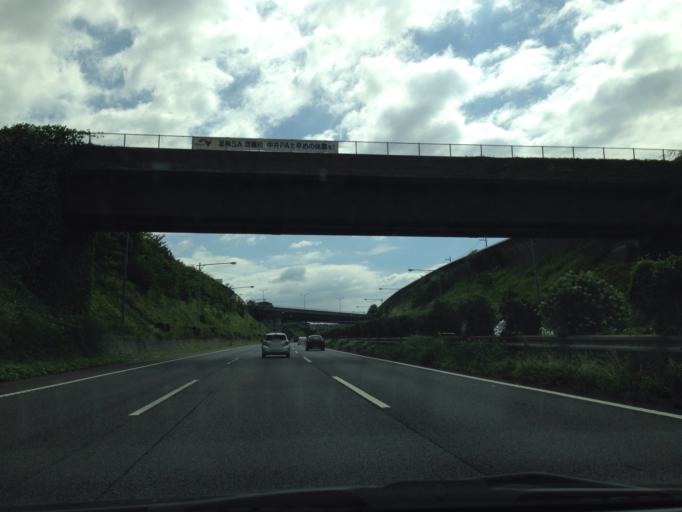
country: JP
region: Kanagawa
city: Hadano
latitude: 35.3656
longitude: 139.2585
